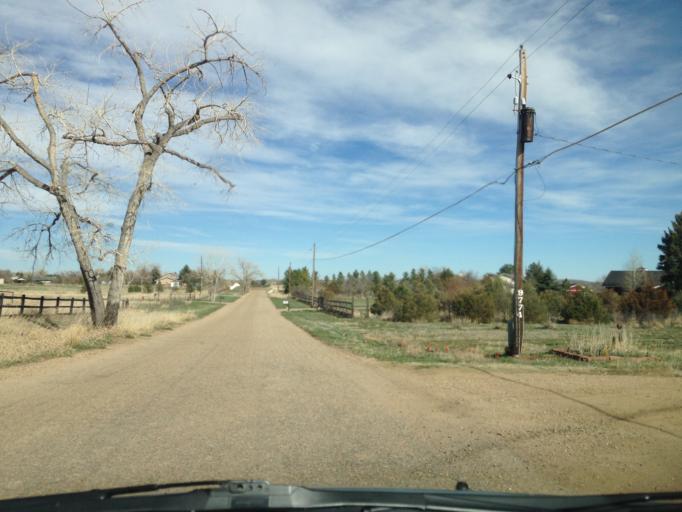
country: US
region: Colorado
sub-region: Boulder County
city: Gunbarrel
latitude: 40.0619
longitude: -105.1247
